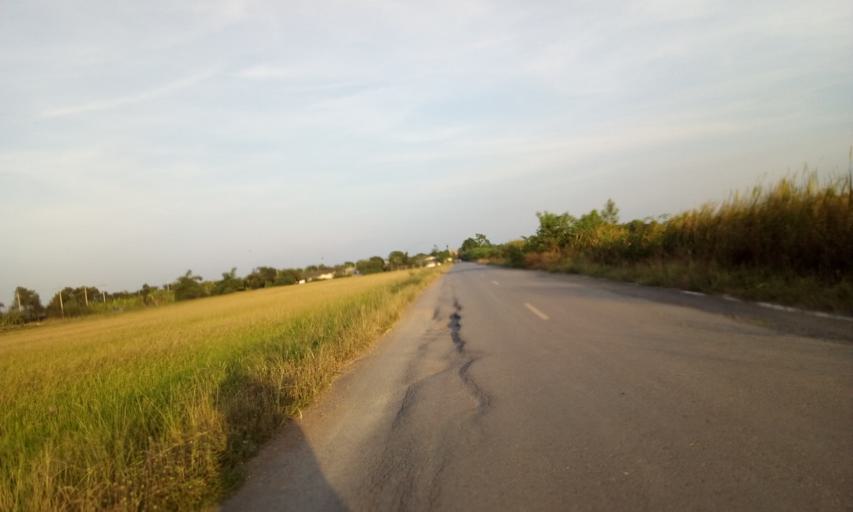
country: TH
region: Pathum Thani
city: Ban Lam Luk Ka
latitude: 14.0369
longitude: 100.8590
